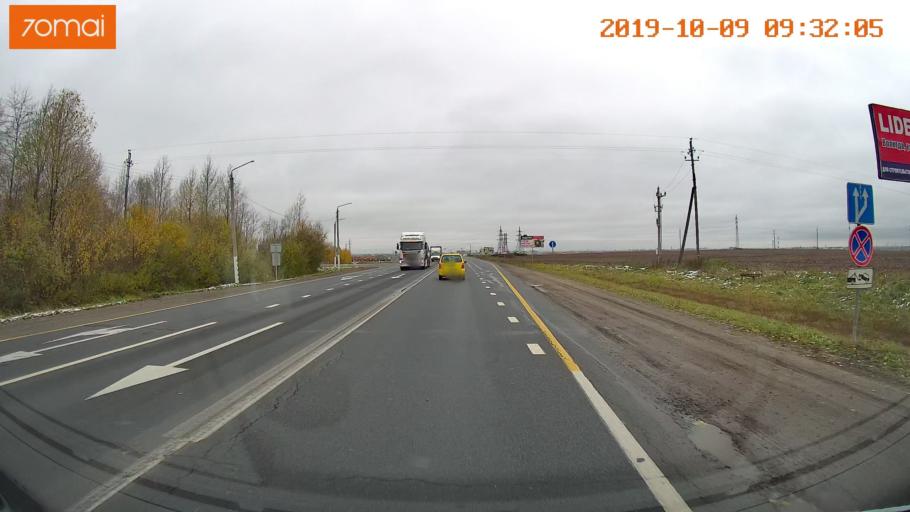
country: RU
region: Vologda
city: Vologda
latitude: 59.1553
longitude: 39.9323
